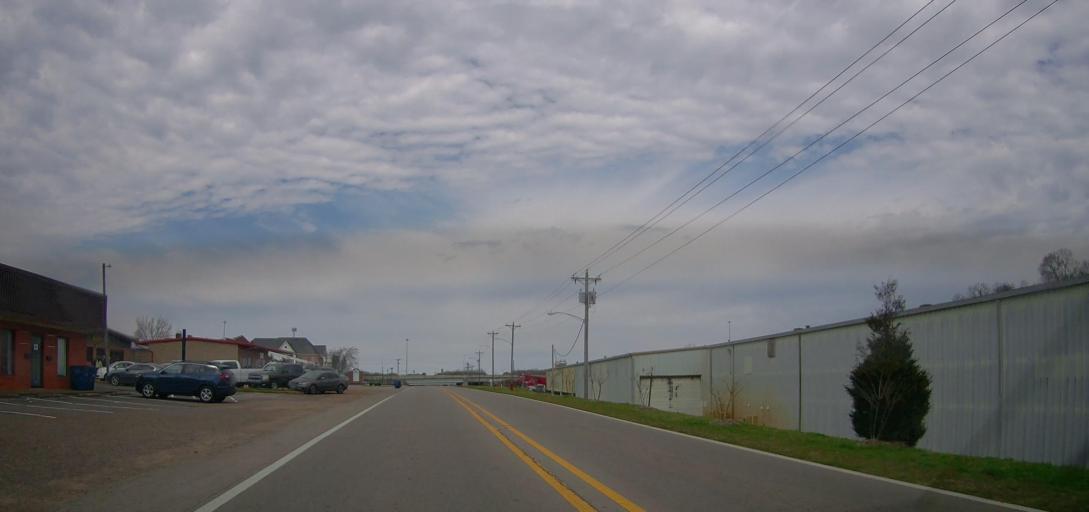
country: US
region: Mississippi
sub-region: De Soto County
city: Olive Branch
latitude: 34.9640
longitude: -89.8277
